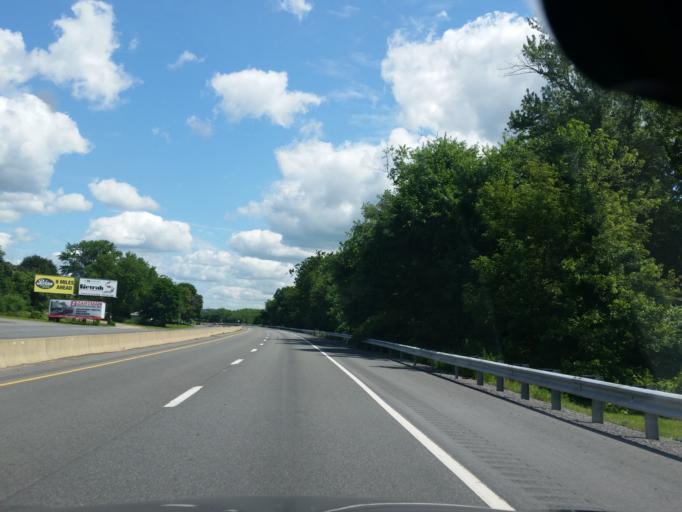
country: US
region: Pennsylvania
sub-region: Snyder County
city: Selinsgrove
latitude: 40.7087
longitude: -76.8633
